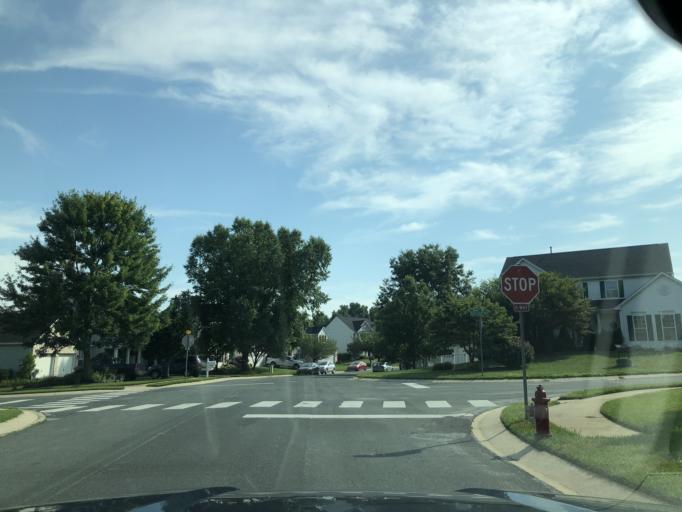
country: US
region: Maryland
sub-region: Carroll County
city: Eldersburg
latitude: 39.4116
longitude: -76.9665
